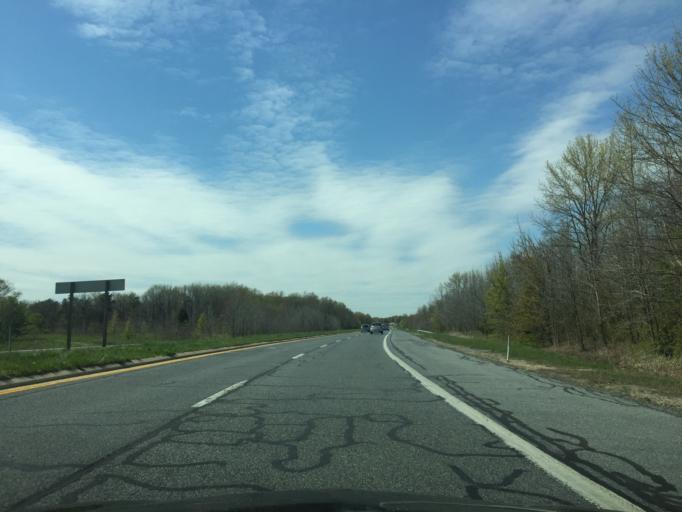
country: US
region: Maryland
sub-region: Baltimore County
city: Middle River
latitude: 39.2939
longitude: -76.4339
